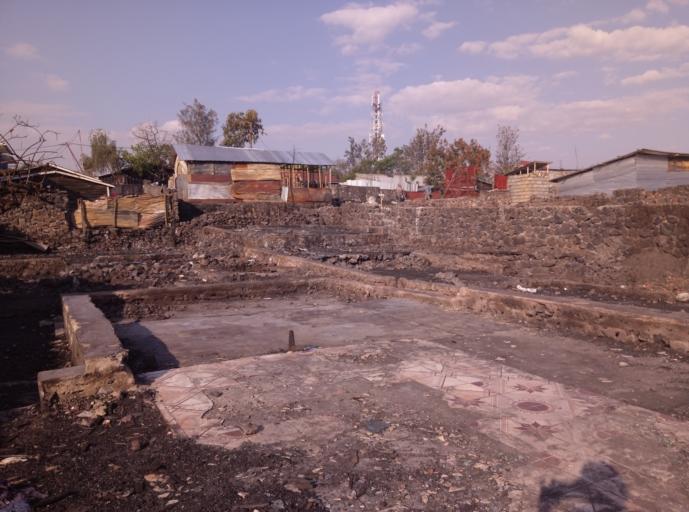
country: CD
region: Nord Kivu
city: Goma
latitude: -1.6595
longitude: 29.2017
